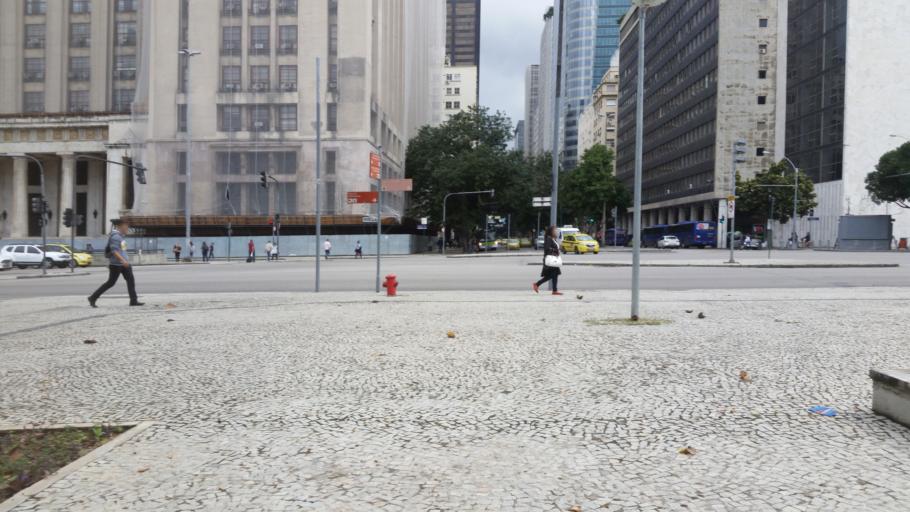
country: BR
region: Rio de Janeiro
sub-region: Rio De Janeiro
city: Rio de Janeiro
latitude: -22.9069
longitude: -43.1727
